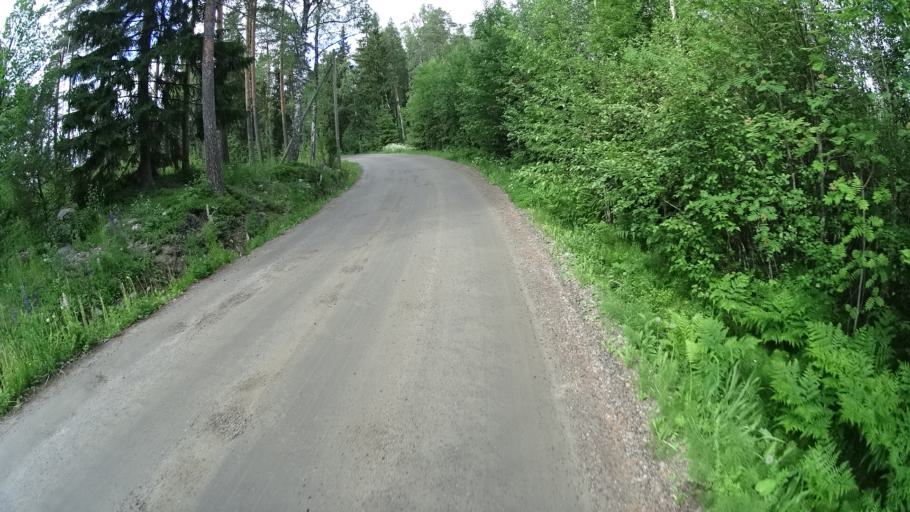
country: FI
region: Uusimaa
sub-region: Helsinki
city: Sibbo
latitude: 60.2826
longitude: 25.3152
